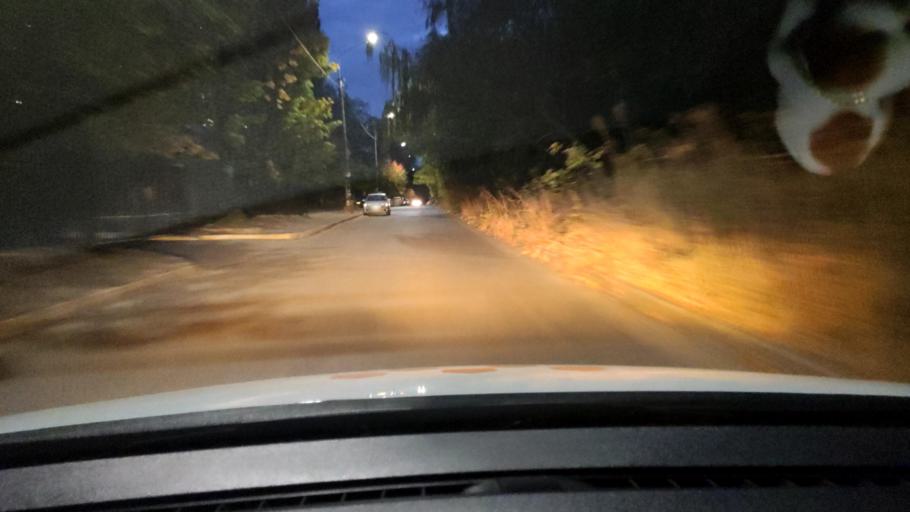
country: RU
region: Voronezj
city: Podgornoye
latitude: 51.7031
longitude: 39.1553
